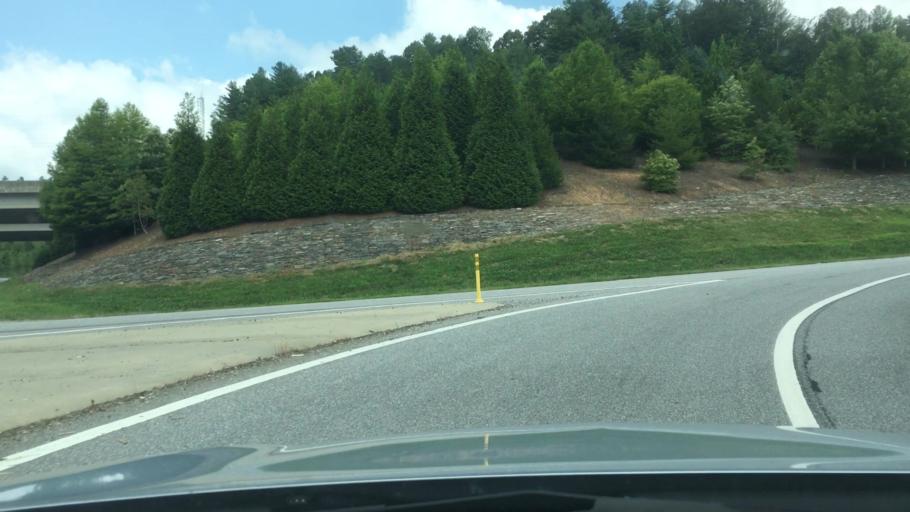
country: US
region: North Carolina
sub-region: Madison County
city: Mars Hill
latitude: 35.8395
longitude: -82.5226
